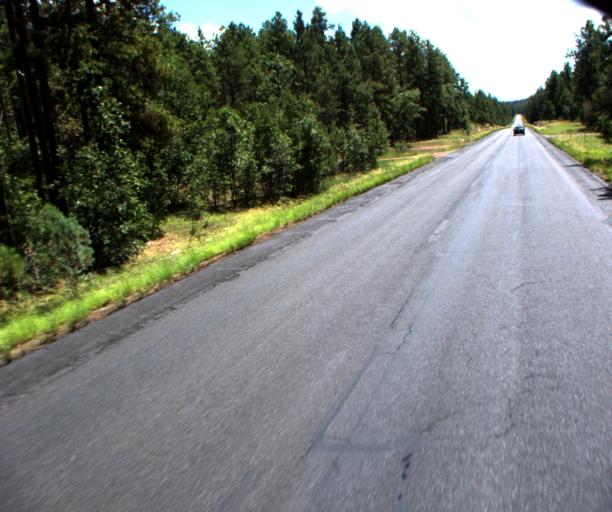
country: US
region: Arizona
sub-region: Gila County
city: Pine
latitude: 34.4826
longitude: -111.4539
